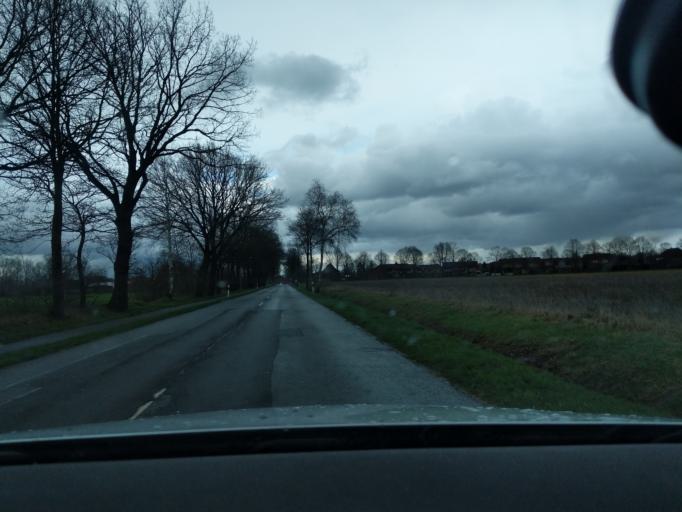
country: DE
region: Lower Saxony
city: Deinste
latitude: 53.5198
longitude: 9.3900
